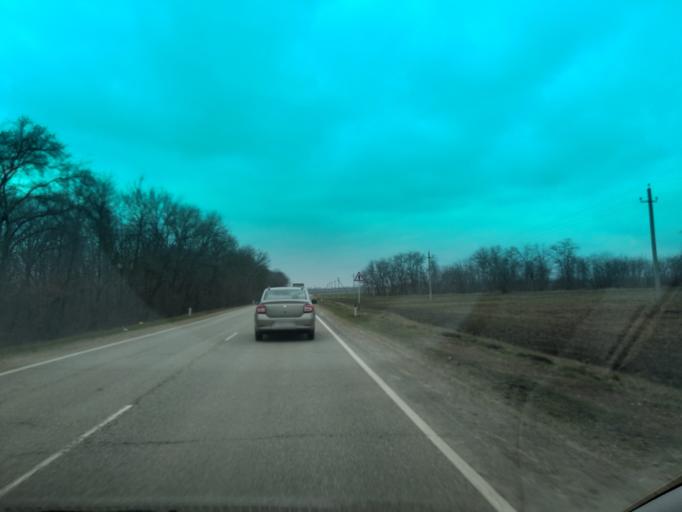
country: RU
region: Krasnodarskiy
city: Novomalorossiyskaya
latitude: 45.7264
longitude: 39.8999
